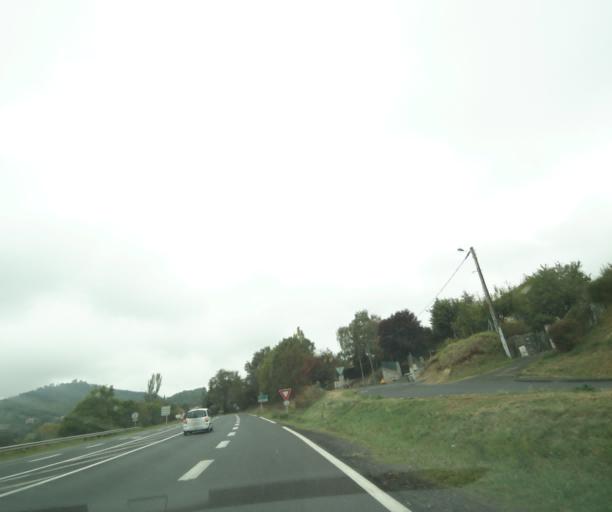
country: FR
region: Auvergne
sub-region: Departement du Puy-de-Dome
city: Ceyrat
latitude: 45.7174
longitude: 3.0695
